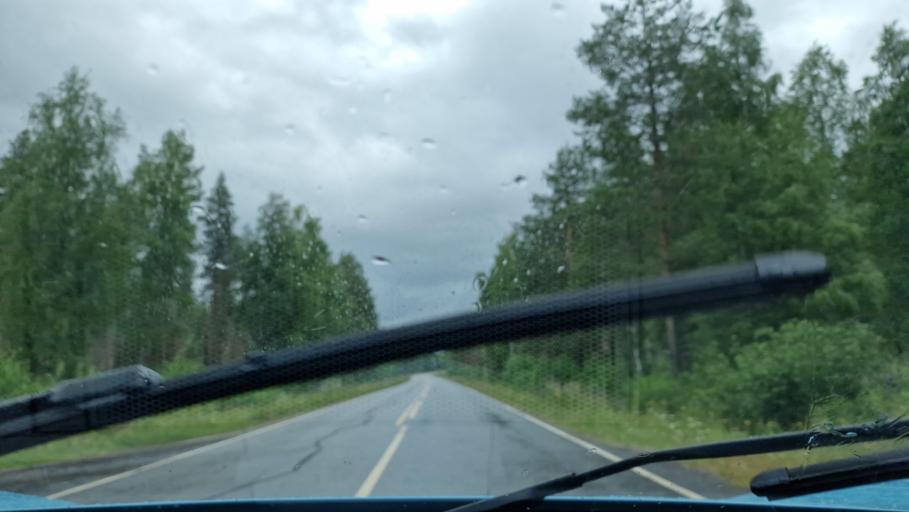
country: FI
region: Southern Ostrobothnia
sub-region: Jaerviseutu
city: Soini
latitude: 62.7779
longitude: 24.3884
